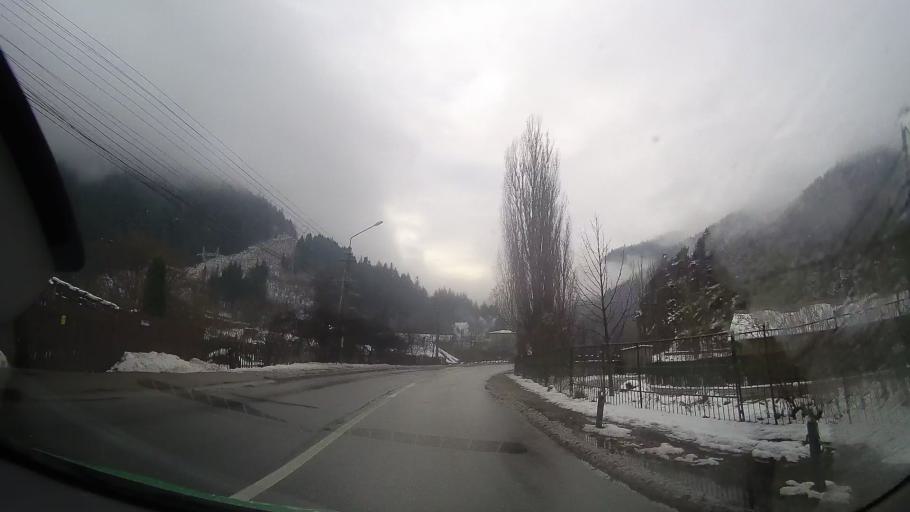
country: RO
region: Neamt
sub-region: Comuna Bicaz
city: Bicaz
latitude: 46.9011
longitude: 26.0726
